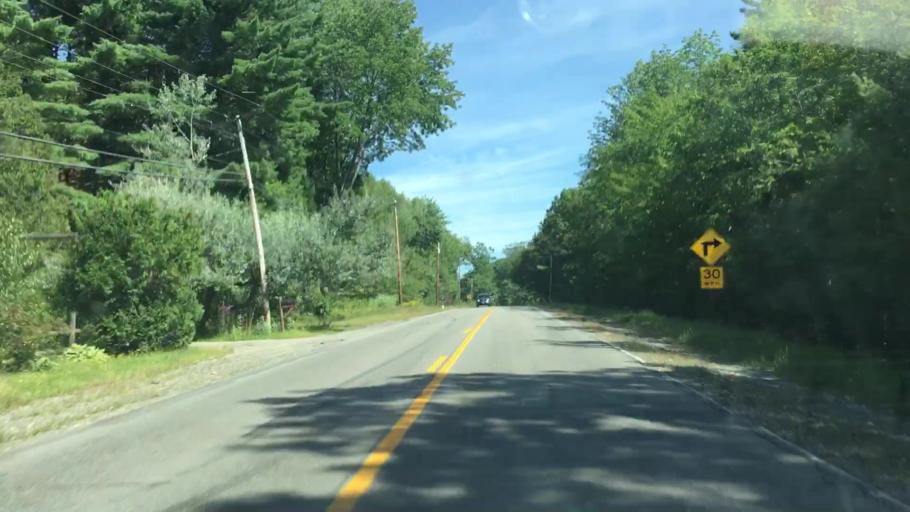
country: US
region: Maine
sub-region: Penobscot County
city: Bradford
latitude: 45.1769
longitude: -68.8574
